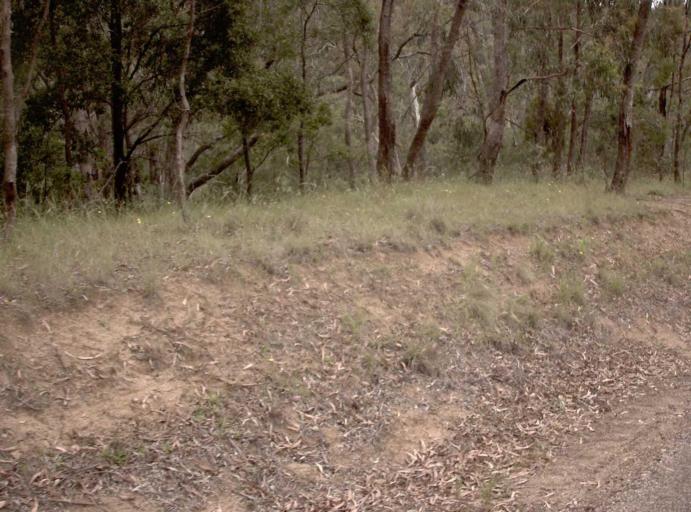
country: AU
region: Victoria
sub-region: East Gippsland
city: Bairnsdale
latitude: -37.5525
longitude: 147.1982
